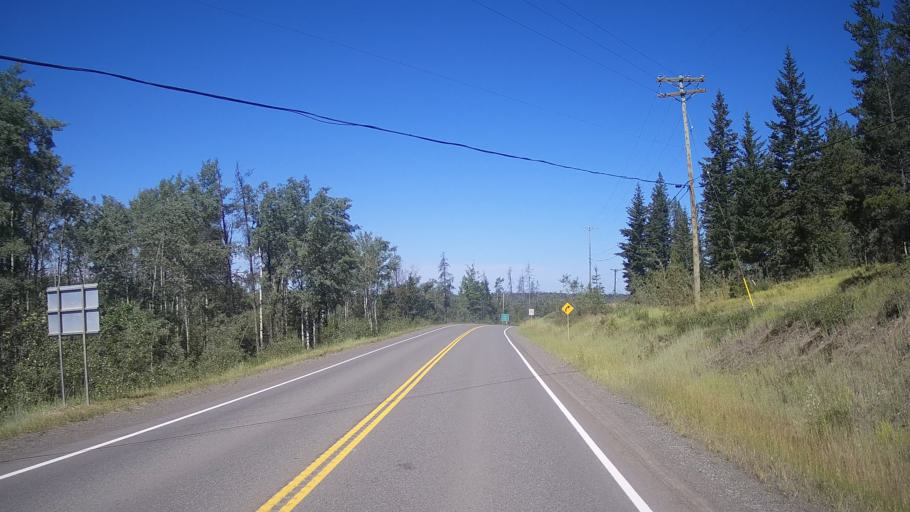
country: CA
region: British Columbia
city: Cache Creek
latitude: 51.5522
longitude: -121.1883
